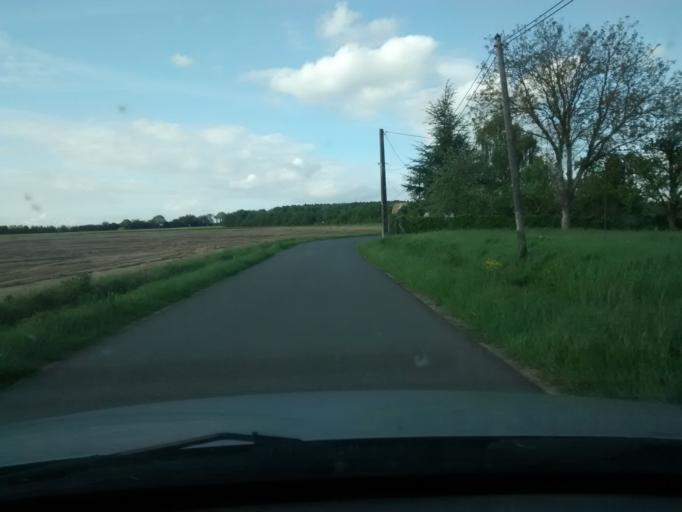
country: FR
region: Pays de la Loire
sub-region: Departement de la Sarthe
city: Challes
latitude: 47.9450
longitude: 0.4319
